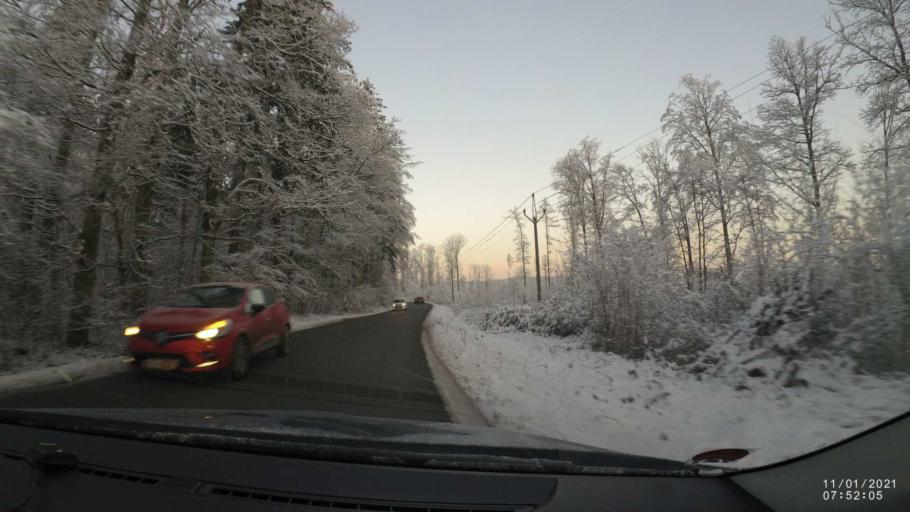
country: CZ
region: South Moravian
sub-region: Okres Blansko
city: Adamov
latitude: 49.2867
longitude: 16.6485
